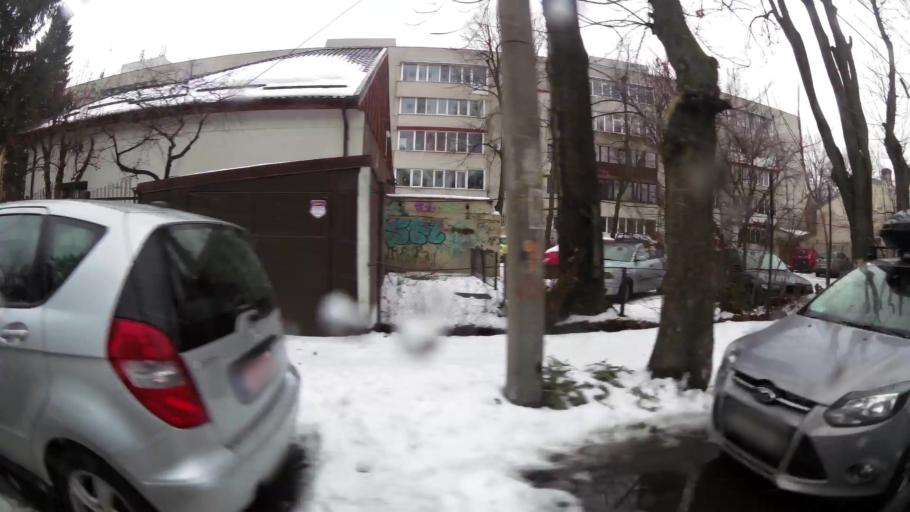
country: RO
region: Ilfov
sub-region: Comuna Chiajna
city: Rosu
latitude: 44.4889
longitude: 26.0384
